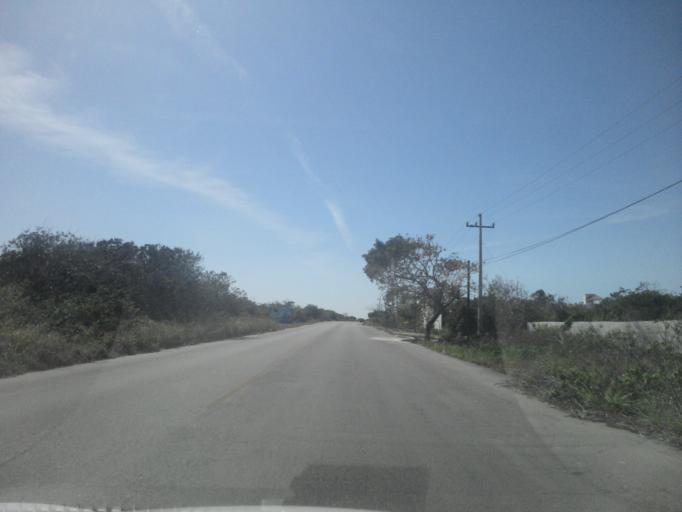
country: MX
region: Yucatan
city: Telchac Puerto
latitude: 21.3295
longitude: -89.3826
